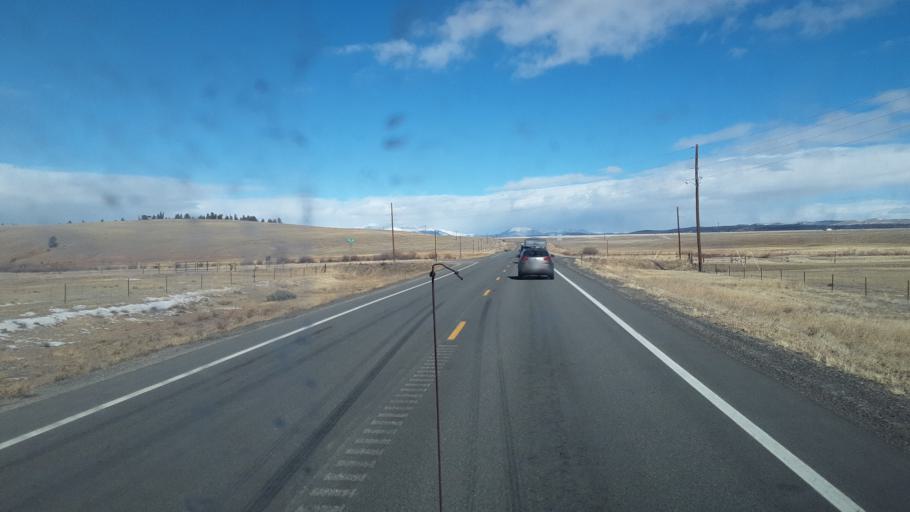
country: US
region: Colorado
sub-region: Park County
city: Fairplay
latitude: 39.0694
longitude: -105.9745
